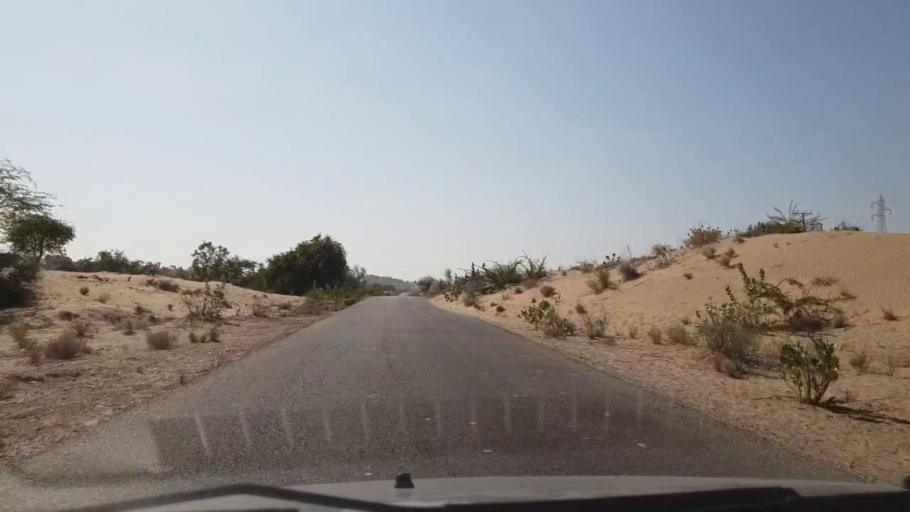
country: PK
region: Sindh
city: Diplo
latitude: 24.5643
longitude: 69.6748
